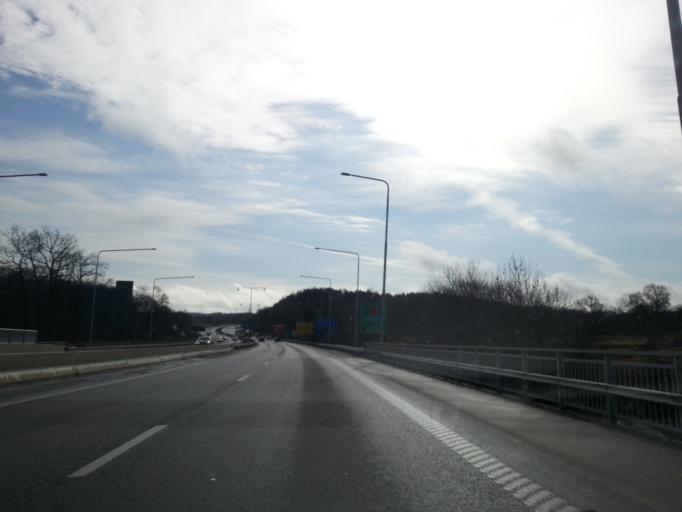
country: SE
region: Vaestra Goetaland
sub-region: Kungalvs Kommun
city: Kungalv
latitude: 57.8622
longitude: 11.9770
